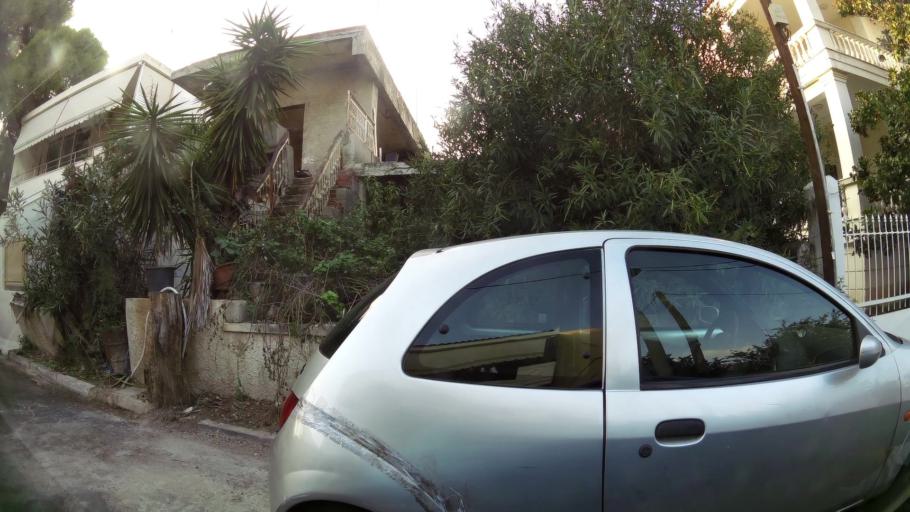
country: GR
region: Attica
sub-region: Nomarchia Athinas
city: Agia Paraskevi
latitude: 38.0164
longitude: 23.8396
